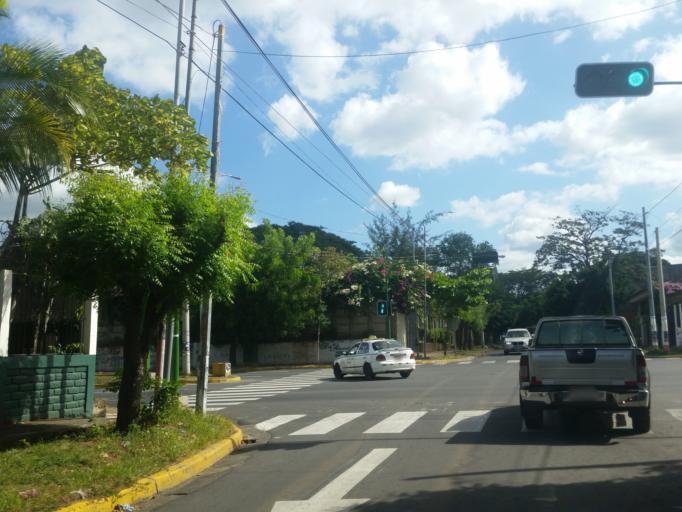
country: NI
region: Managua
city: Managua
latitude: 12.1221
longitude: -86.2694
